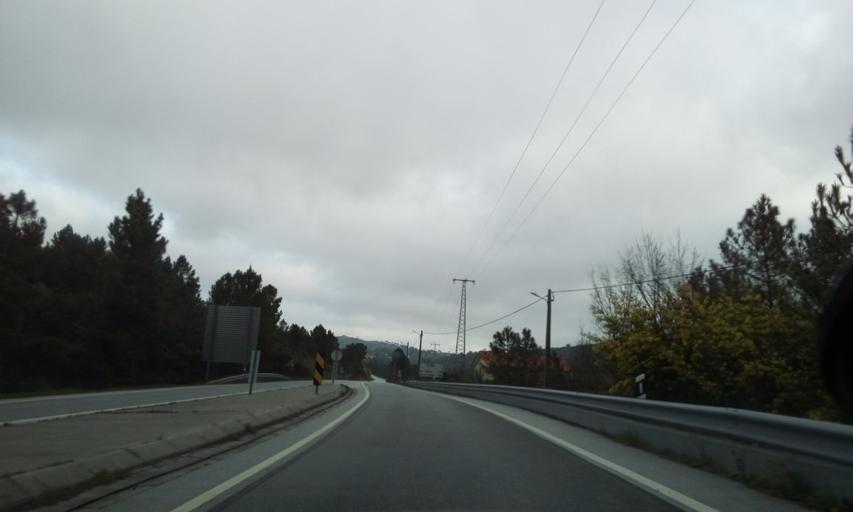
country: PT
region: Guarda
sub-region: Fornos de Algodres
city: Fornos de Algodres
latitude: 40.6385
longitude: -7.4955
